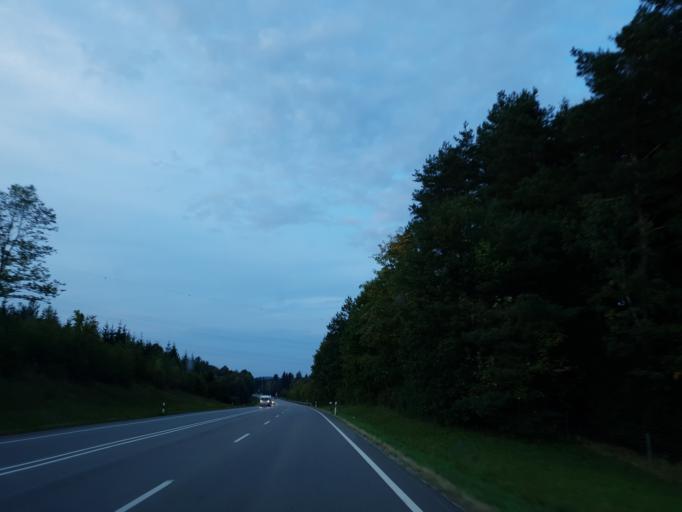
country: DE
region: Bavaria
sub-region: Swabia
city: Biessenhofen
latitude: 47.8226
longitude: 10.6707
